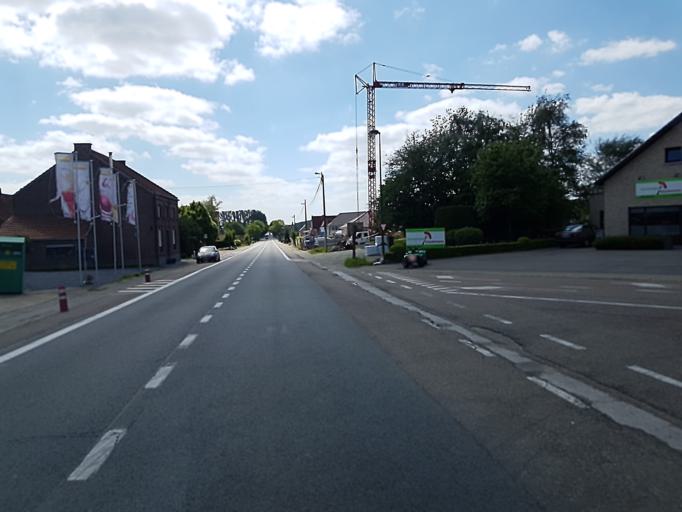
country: BE
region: Flanders
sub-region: Provincie Vlaams-Brabant
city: Glabbeek-Zuurbemde
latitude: 50.8636
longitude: 4.9565
